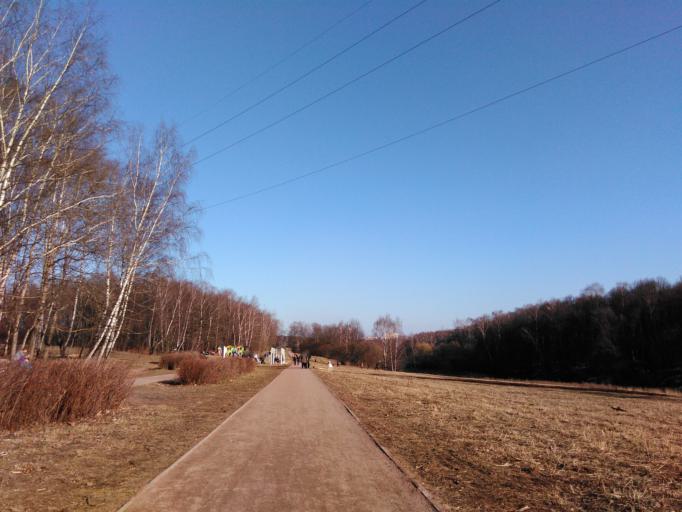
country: RU
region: Moscow
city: Zyuzino
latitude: 55.6371
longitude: 37.5474
